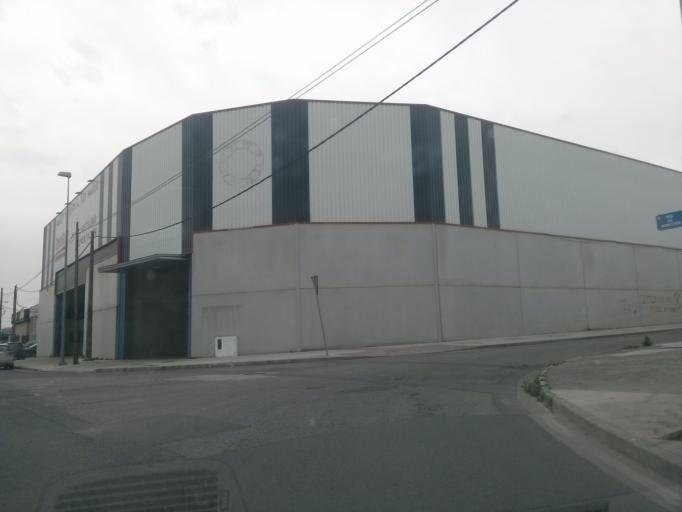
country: ES
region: Galicia
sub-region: Provincia de Lugo
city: Lugo
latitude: 43.0479
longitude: -7.5741
